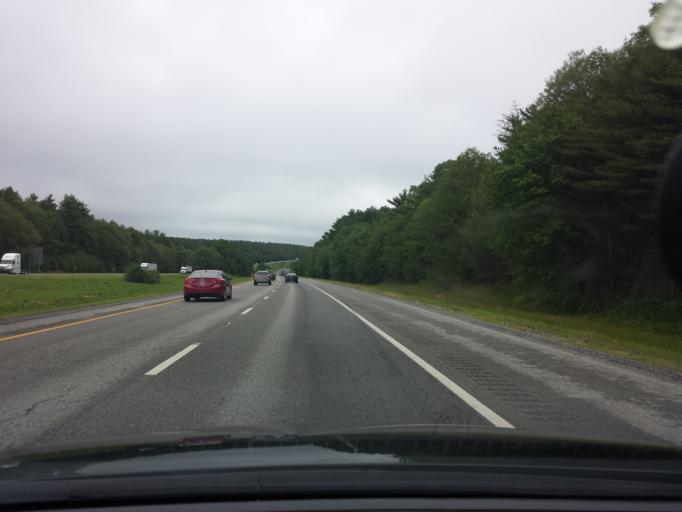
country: US
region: Rhode Island
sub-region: Kent County
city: West Greenwich
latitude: 41.6223
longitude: -71.6421
